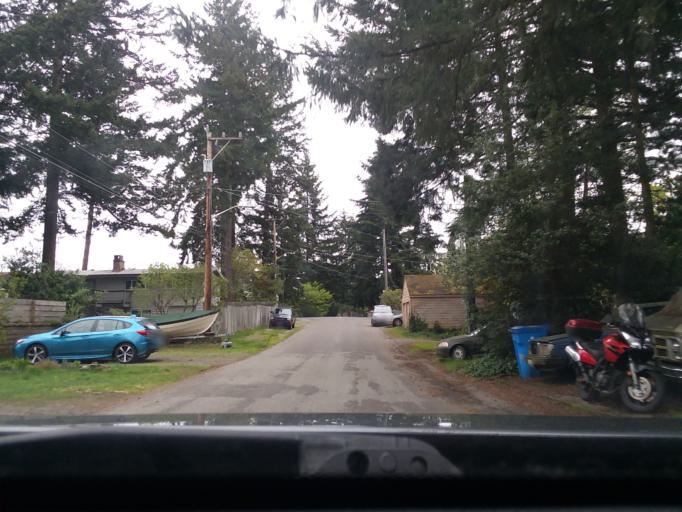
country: US
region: Washington
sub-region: King County
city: Shoreline
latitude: 47.7359
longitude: -122.3489
